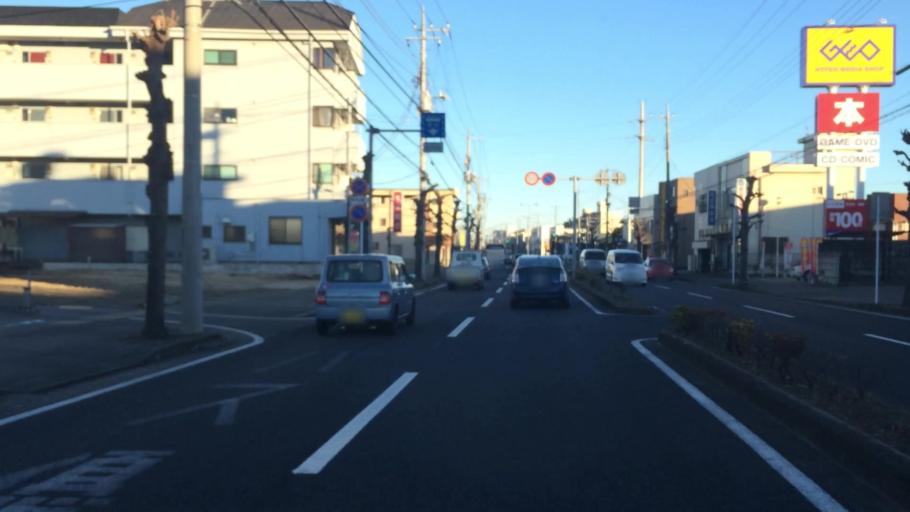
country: JP
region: Tochigi
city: Utsunomiya-shi
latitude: 36.5492
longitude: 139.9225
